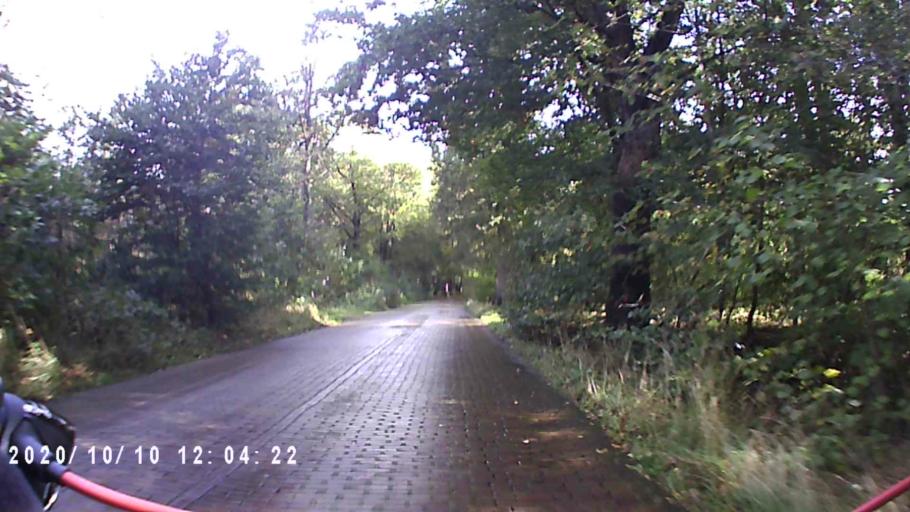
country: NL
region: Friesland
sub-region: Gemeente Heerenveen
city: Jubbega
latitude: 53.0582
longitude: 6.1282
